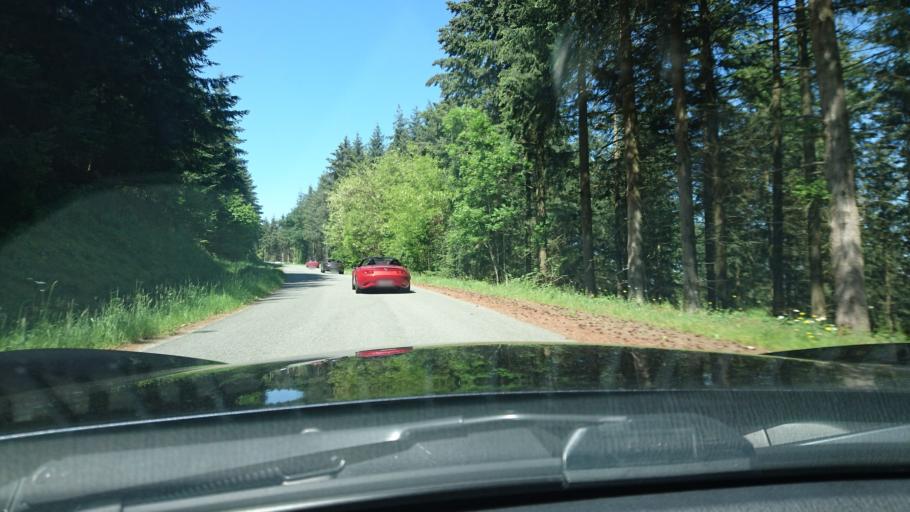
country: FR
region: Rhone-Alpes
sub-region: Departement de la Loire
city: Bussieres
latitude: 45.8616
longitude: 4.2473
